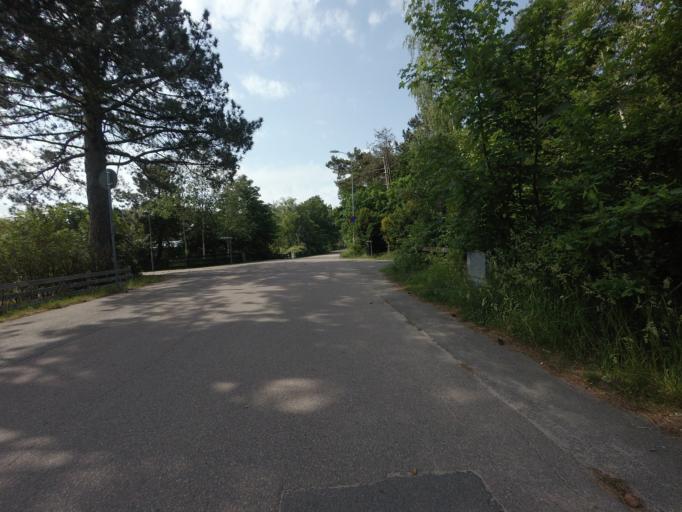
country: SE
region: Skane
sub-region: Angelholms Kommun
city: AEngelholm
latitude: 56.2586
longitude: 12.8358
